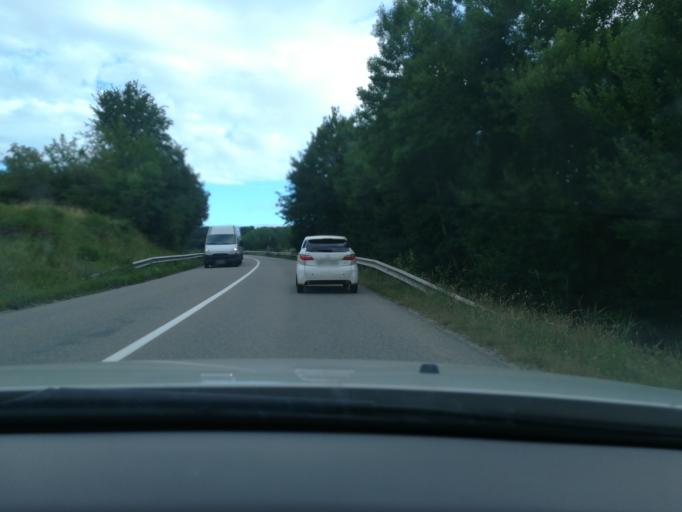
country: FR
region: Alsace
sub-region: Departement du Bas-Rhin
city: Bouxwiller
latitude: 48.8332
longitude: 7.4922
